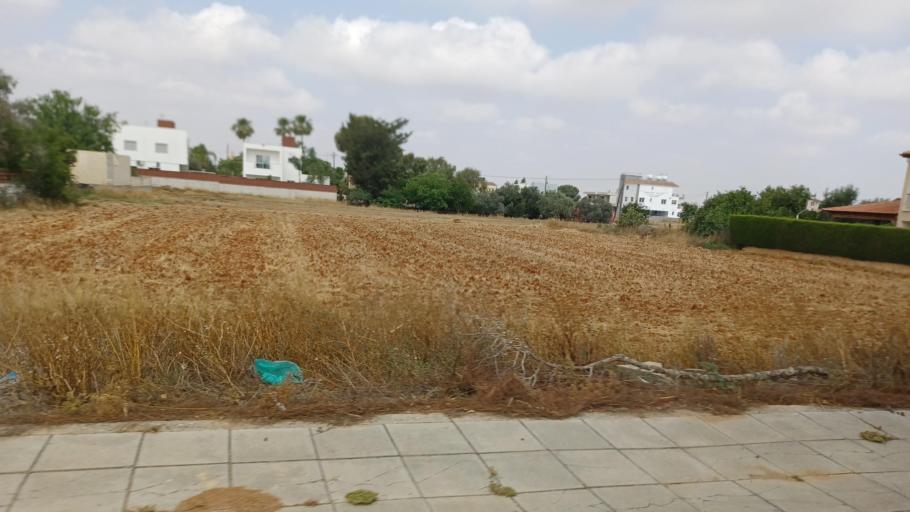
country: CY
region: Ammochostos
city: Deryneia
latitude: 35.0557
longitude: 33.9566
